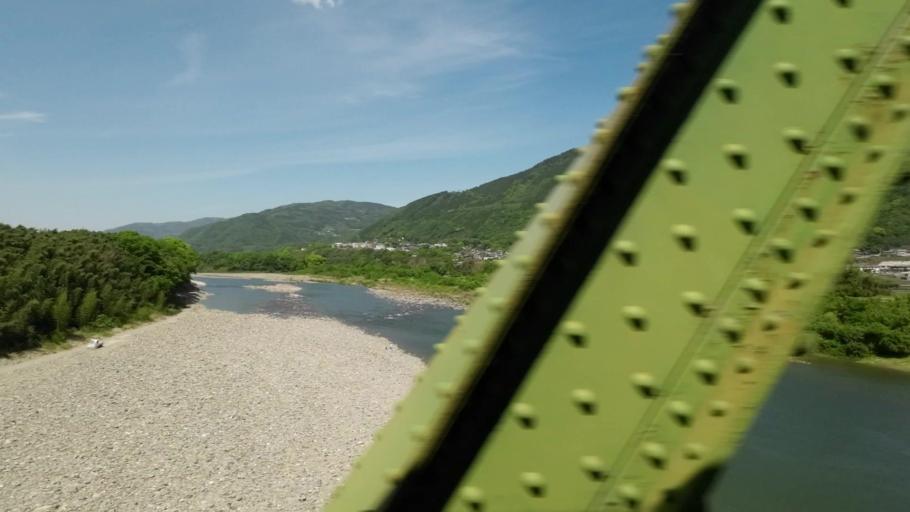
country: JP
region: Tokushima
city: Ikedacho
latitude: 34.0355
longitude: 133.8636
